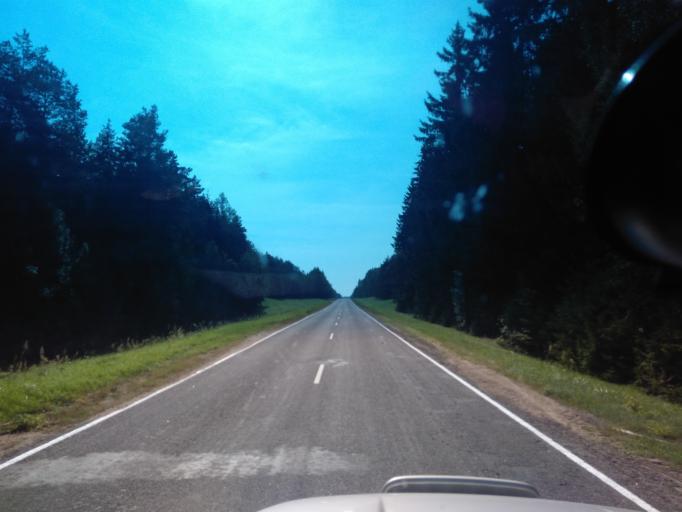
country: BY
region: Minsk
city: Uzda
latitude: 53.3278
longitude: 27.2313
